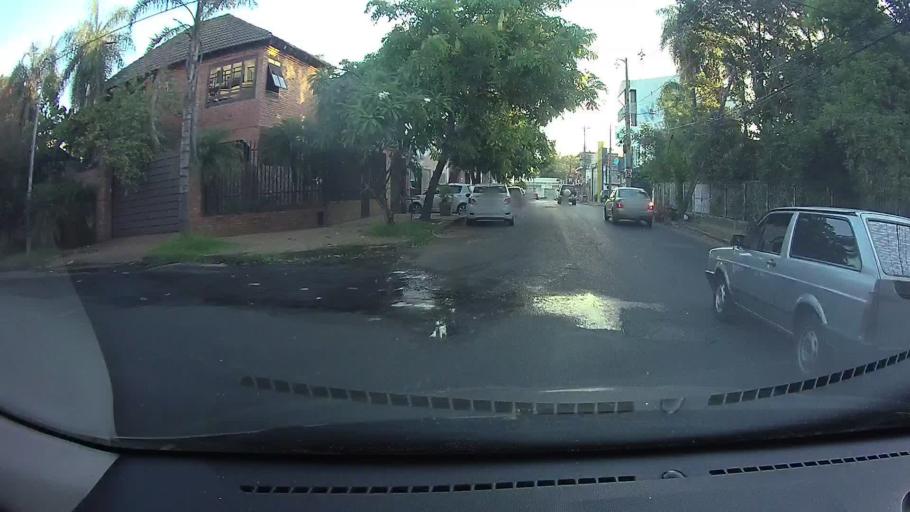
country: PY
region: Central
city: Lambare
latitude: -25.3129
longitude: -57.5800
